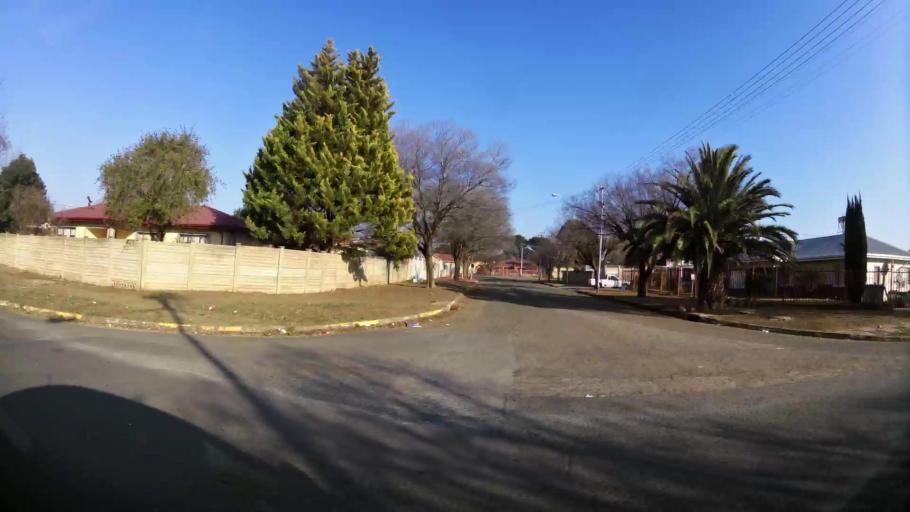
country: ZA
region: Orange Free State
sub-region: Mangaung Metropolitan Municipality
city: Bloemfontein
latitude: -29.1466
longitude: 26.2139
